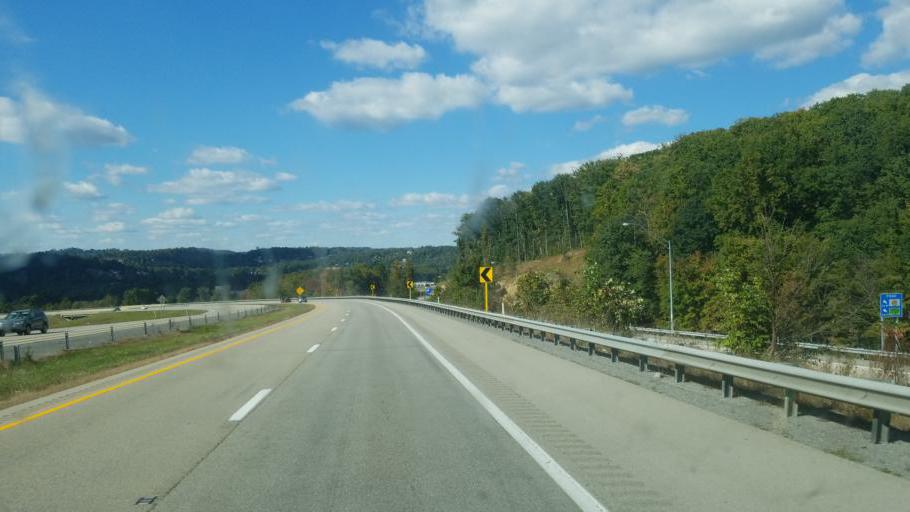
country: US
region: West Virginia
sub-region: Monongalia County
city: Cheat Lake
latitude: 39.6683
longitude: -79.8473
